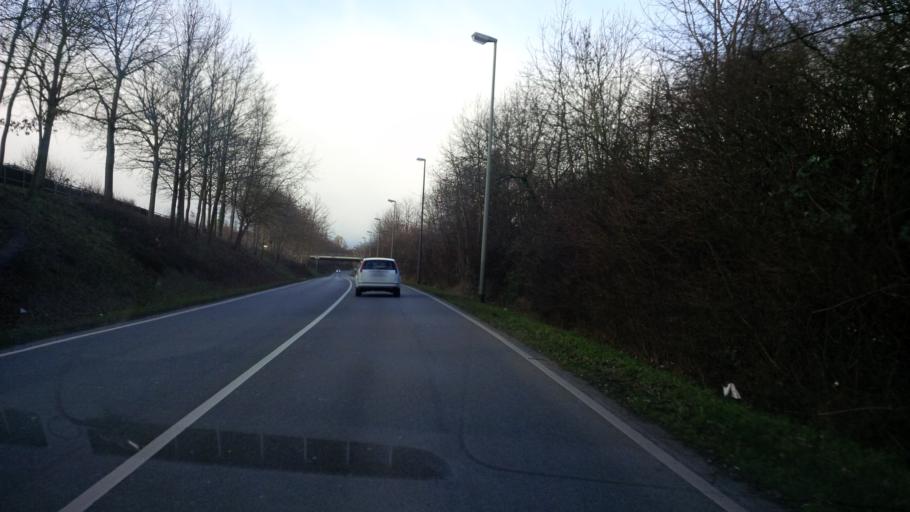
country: DE
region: Hesse
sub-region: Regierungsbezirk Darmstadt
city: Frankfurt am Main
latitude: 50.1456
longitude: 8.6815
